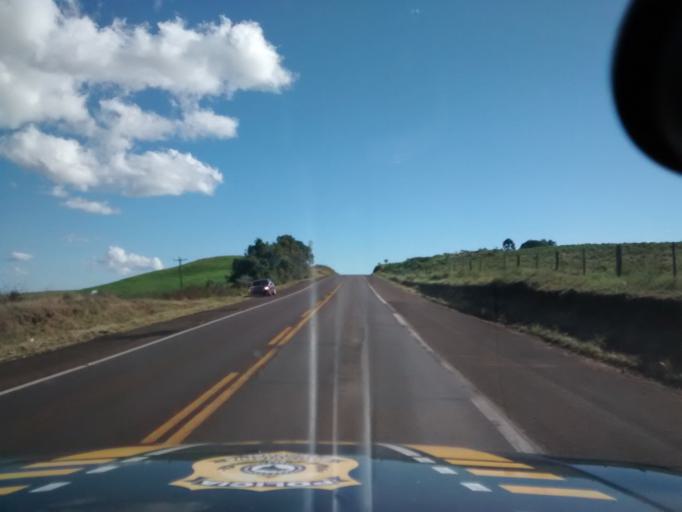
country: BR
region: Rio Grande do Sul
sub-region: Lagoa Vermelha
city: Lagoa Vermelha
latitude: -28.3253
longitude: -51.2584
